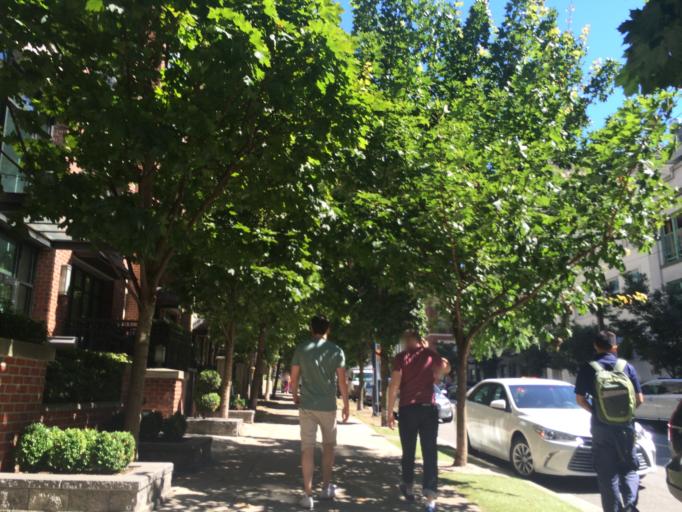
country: CA
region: British Columbia
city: West End
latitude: 49.2747
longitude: -123.1241
